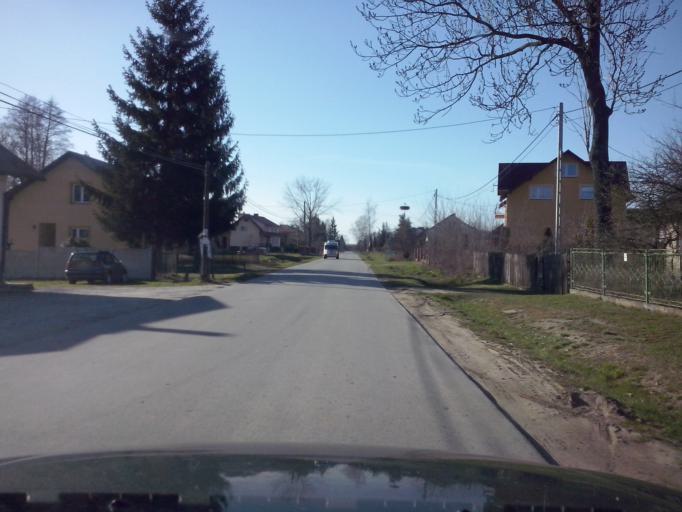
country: PL
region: Subcarpathian Voivodeship
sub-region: Powiat nizanski
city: Krzeszow
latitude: 50.3801
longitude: 22.3899
